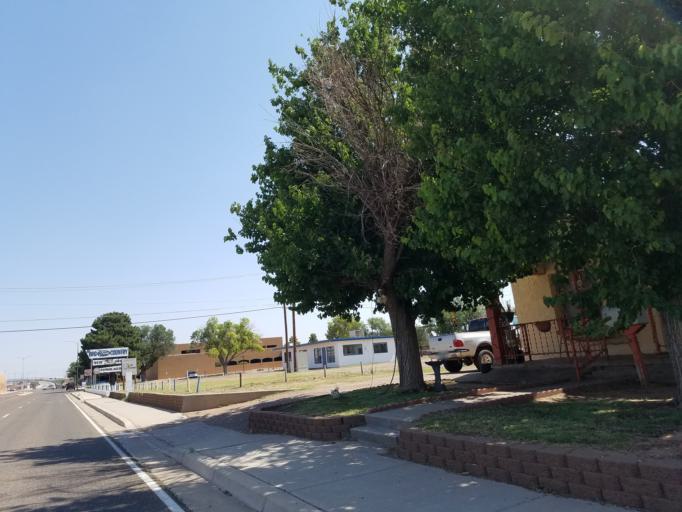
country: US
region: New Mexico
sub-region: Quay County
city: Tucumcari
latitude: 35.1747
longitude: -103.7248
